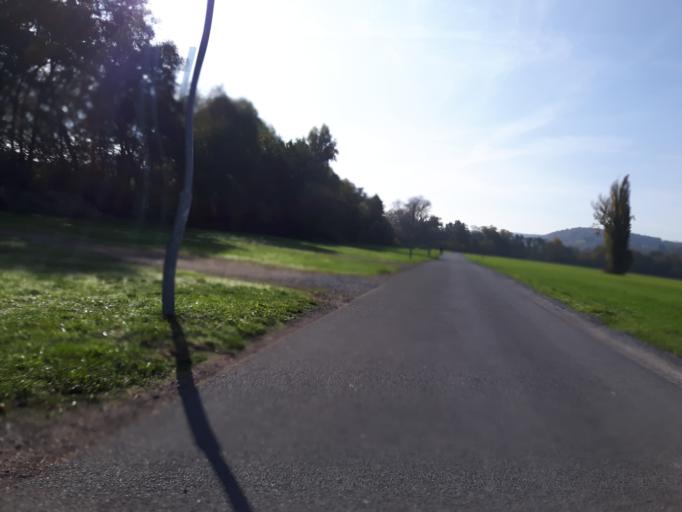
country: DE
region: Bavaria
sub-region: Regierungsbezirk Unterfranken
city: Obernburg am Main
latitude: 49.8355
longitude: 9.1468
